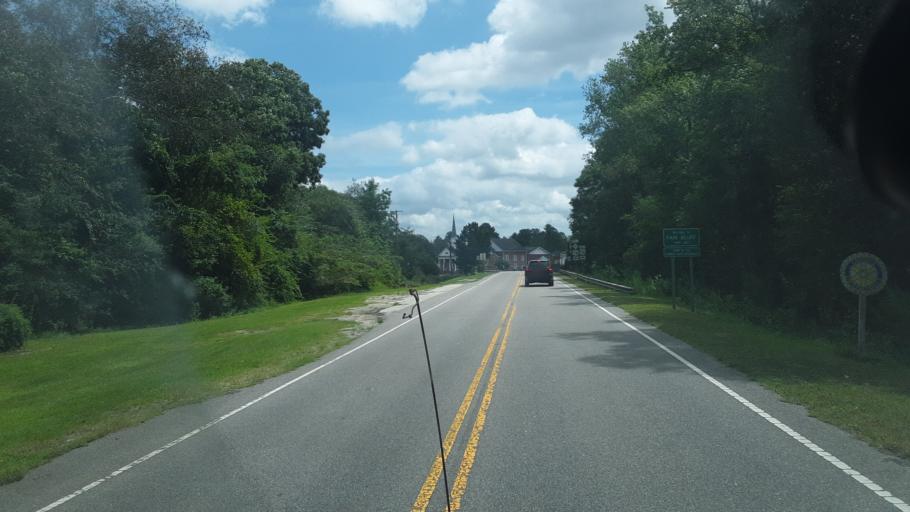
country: US
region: North Carolina
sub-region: Robeson County
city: Fairmont
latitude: 34.3140
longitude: -79.0393
